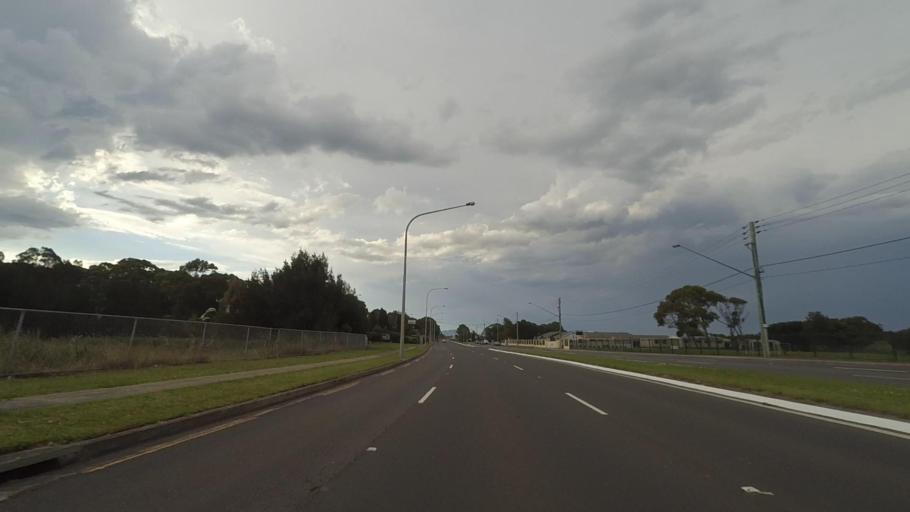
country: AU
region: New South Wales
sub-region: Shellharbour
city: Shellharbour Village
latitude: -34.5747
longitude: 150.8639
